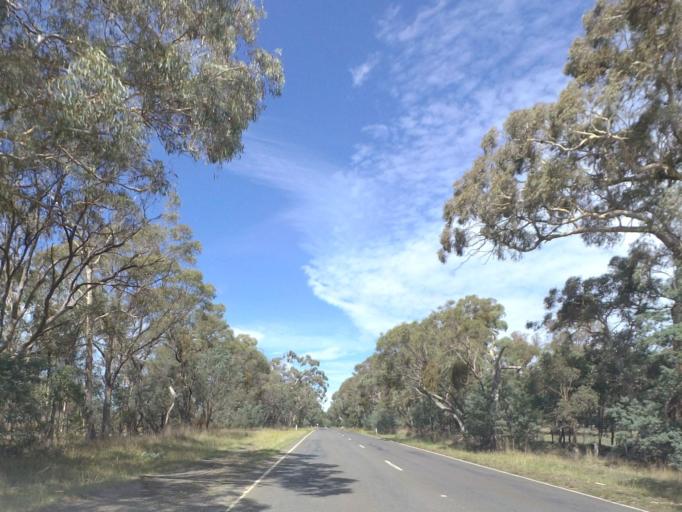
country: AU
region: Victoria
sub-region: Hume
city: Sunbury
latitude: -37.2967
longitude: 144.5107
